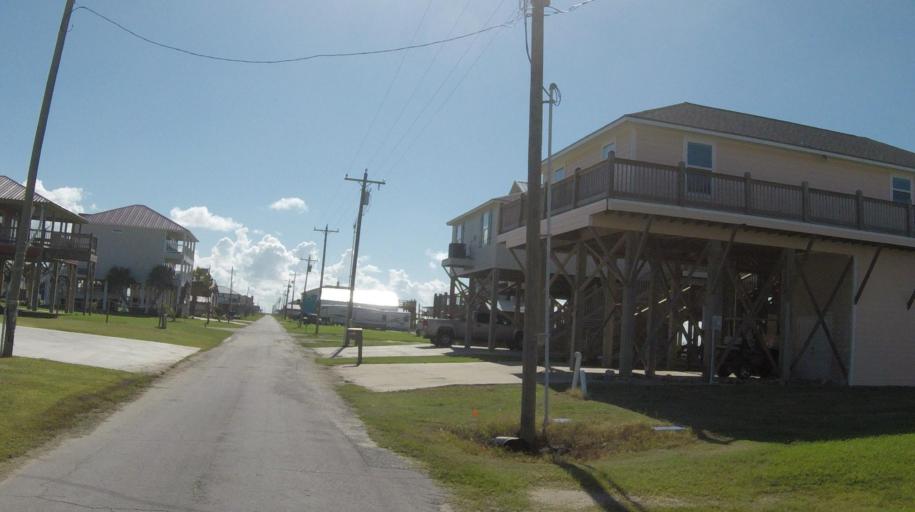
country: US
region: Louisiana
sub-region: Cameron Parish
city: Cameron
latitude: 29.7706
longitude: -93.4576
